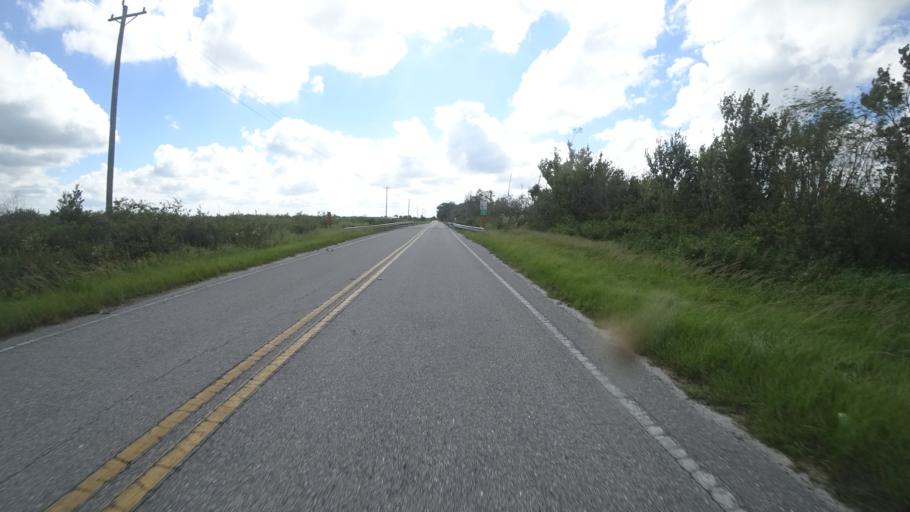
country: US
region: Florida
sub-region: Sarasota County
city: Lake Sarasota
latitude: 27.4060
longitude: -82.1327
